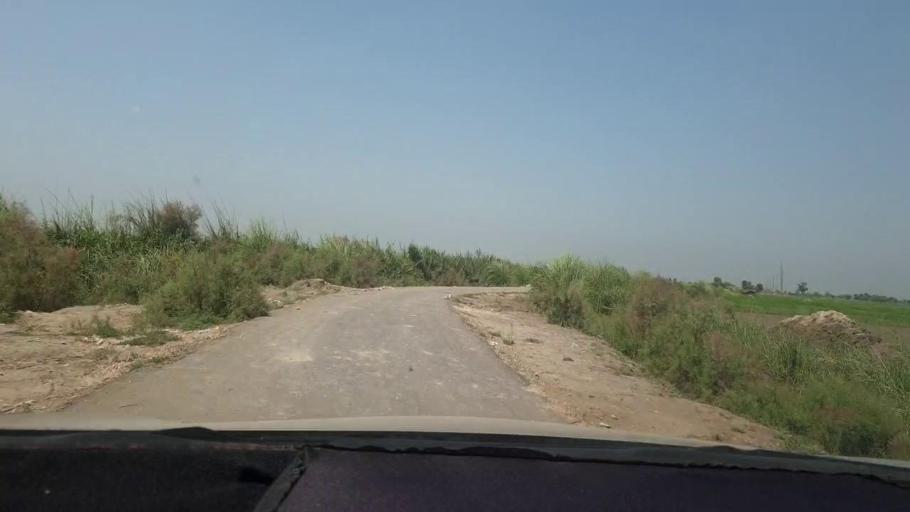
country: PK
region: Sindh
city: Shahdadkot
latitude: 27.8358
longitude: 67.8774
